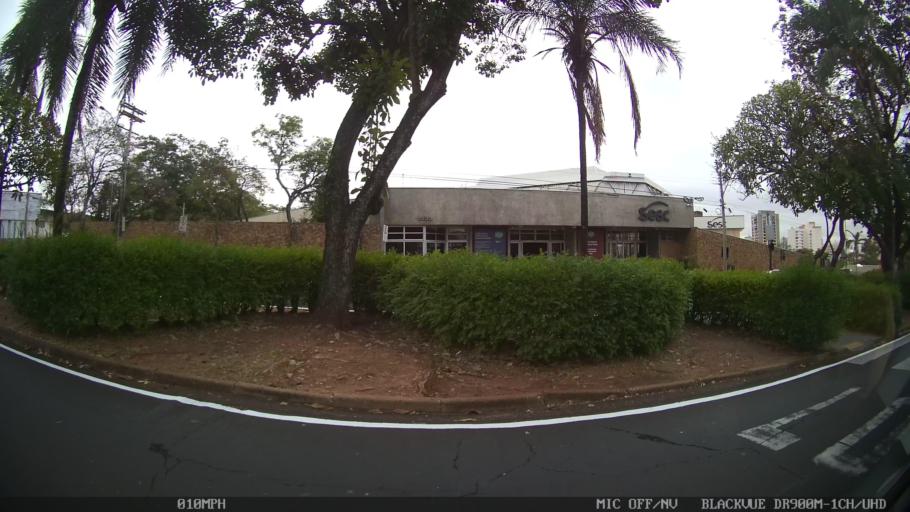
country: BR
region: Sao Paulo
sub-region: Sao Jose Do Rio Preto
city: Sao Jose do Rio Preto
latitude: -20.8342
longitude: -49.3943
